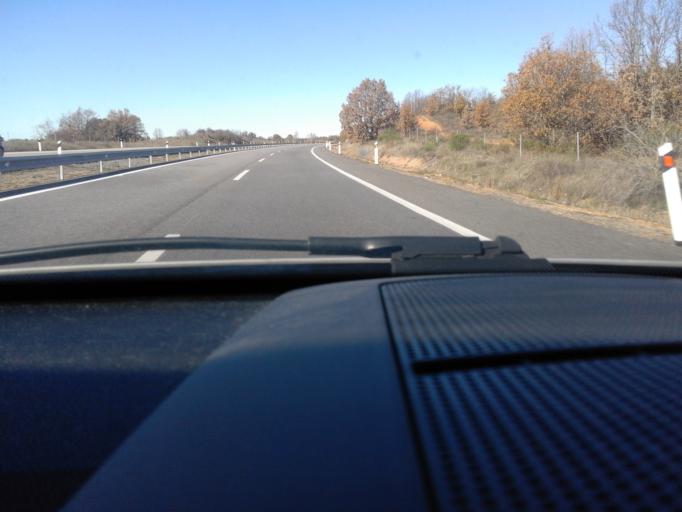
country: ES
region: Castille and Leon
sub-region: Provincia de Leon
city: Valverde de la Virgen
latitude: 42.6000
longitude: -5.7056
